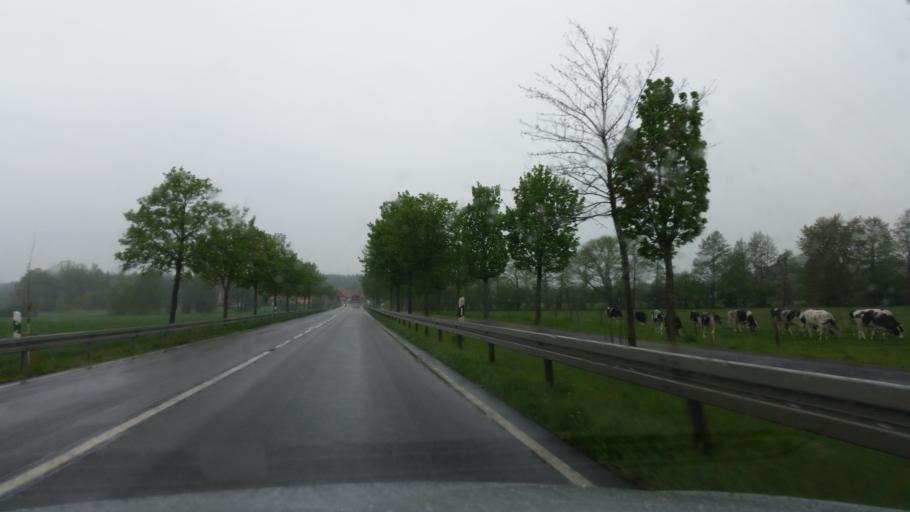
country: DE
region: Saxony-Anhalt
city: Gardelegen
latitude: 52.5495
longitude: 11.3642
